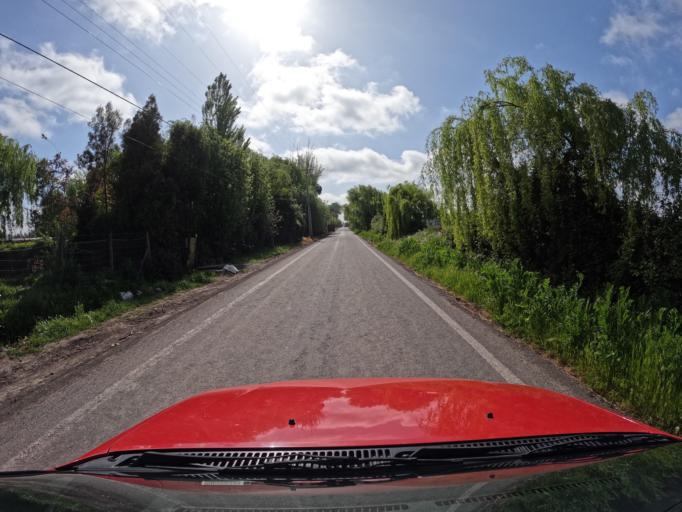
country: CL
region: Maule
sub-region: Provincia de Curico
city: Rauco
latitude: -34.8879
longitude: -71.2681
